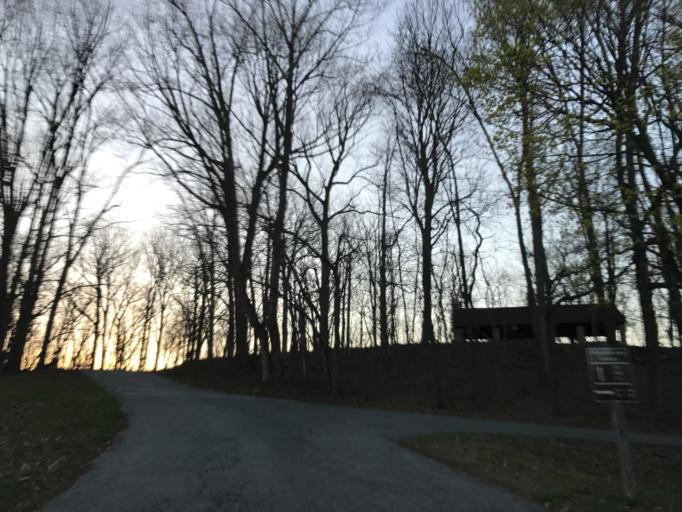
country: US
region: Maryland
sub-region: Carroll County
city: Eldersburg
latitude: 39.3601
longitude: -76.8870
